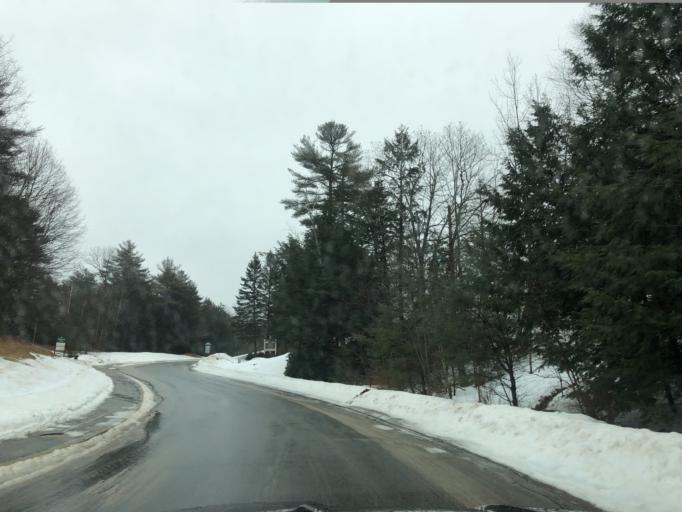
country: US
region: Maine
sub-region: Cumberland County
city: Falmouth Foreside
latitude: 43.7360
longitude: -70.2217
